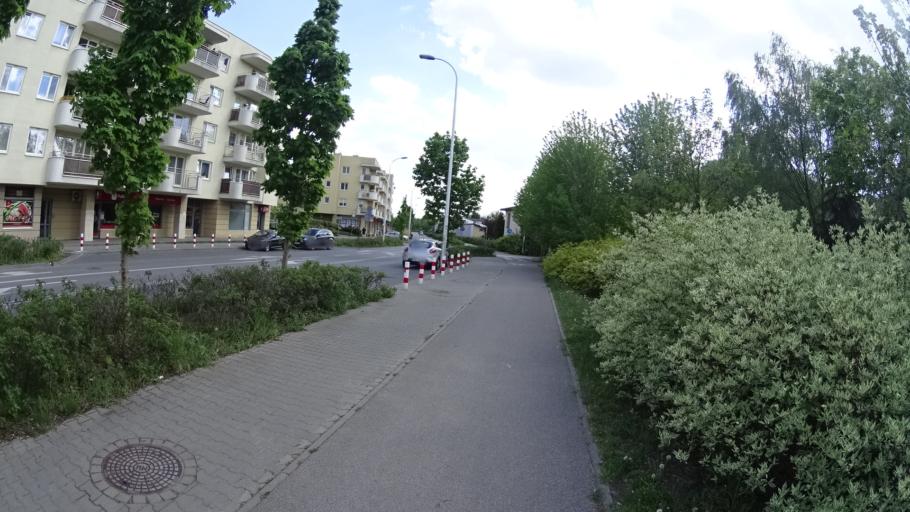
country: PL
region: Masovian Voivodeship
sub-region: Warszawa
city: Mokotow
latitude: 52.2127
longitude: 21.0587
